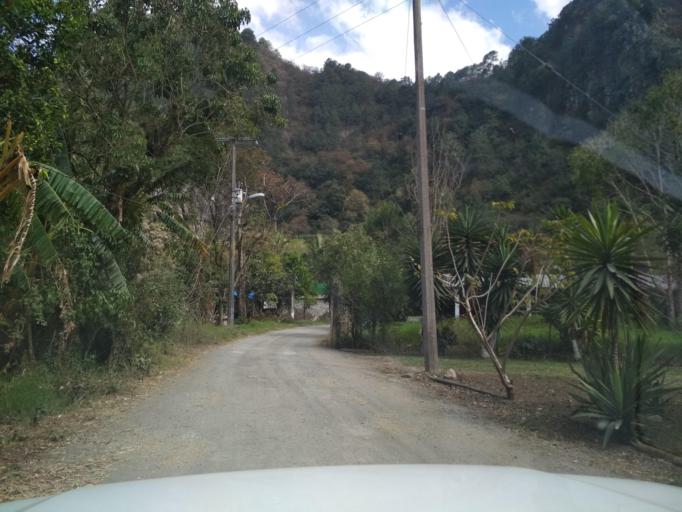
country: MX
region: Veracruz
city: Jalapilla
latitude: 18.7978
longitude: -97.1021
